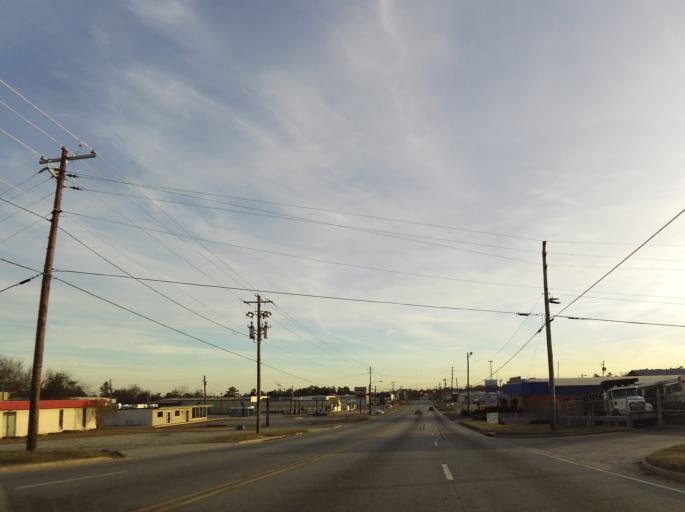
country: US
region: Georgia
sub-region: Bibb County
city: Macon
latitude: 32.8094
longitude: -83.6403
